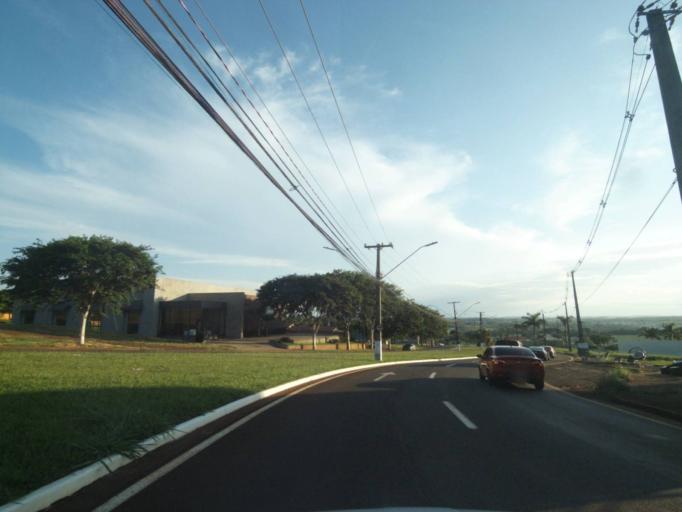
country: BR
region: Parana
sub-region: Londrina
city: Londrina
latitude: -23.3444
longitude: -51.1889
